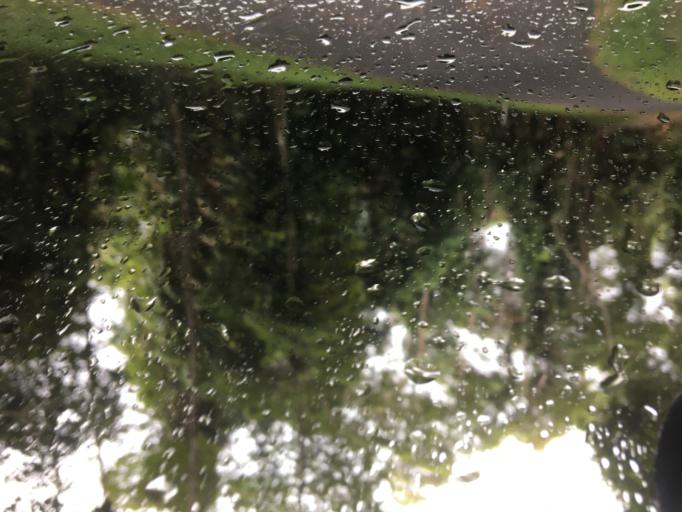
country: AU
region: Queensland
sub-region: Tablelands
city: Kuranda
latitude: -16.8383
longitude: 145.6418
